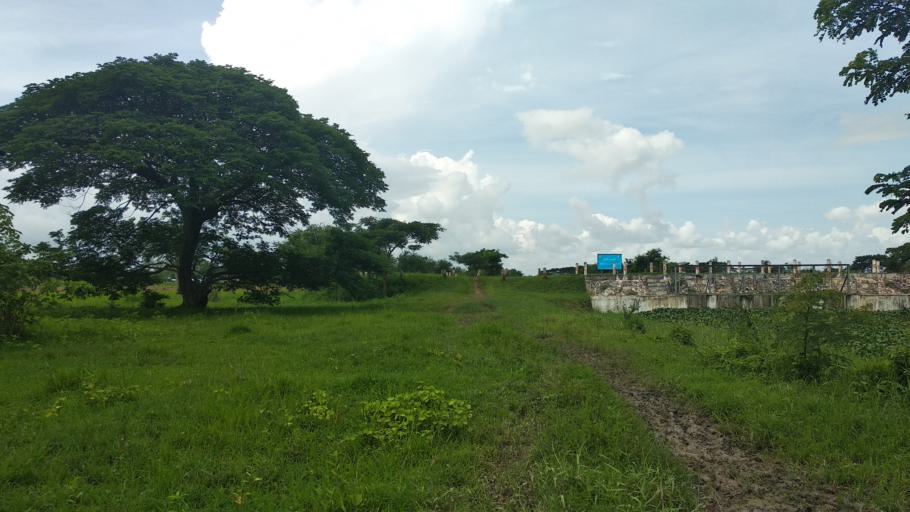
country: MM
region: Yangon
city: Kanbe
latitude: 16.8806
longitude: 95.9753
